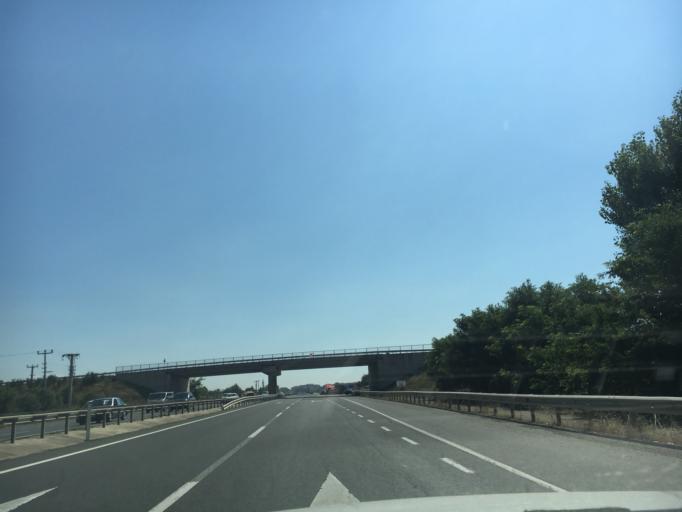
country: TR
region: Tekirdag
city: Marmara Ereglisi
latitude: 40.9721
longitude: 27.9345
